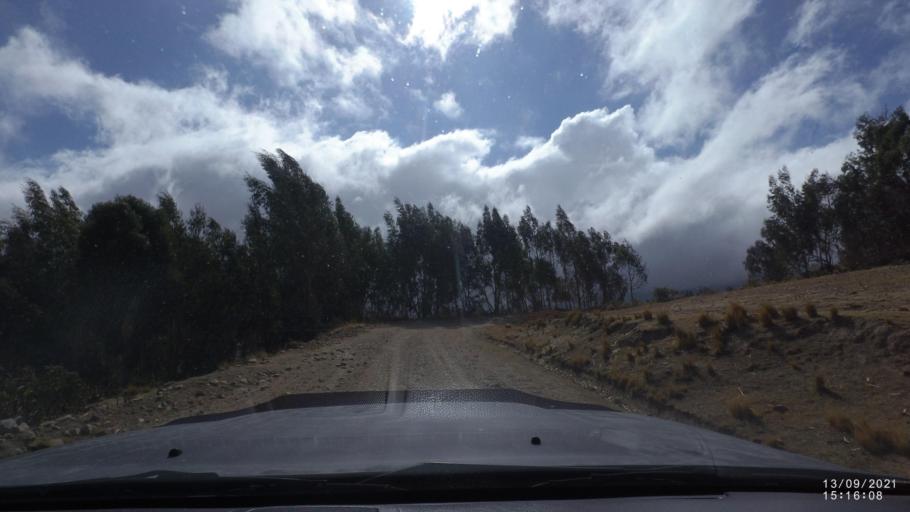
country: BO
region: Cochabamba
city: Colomi
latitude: -17.3667
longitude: -65.7941
